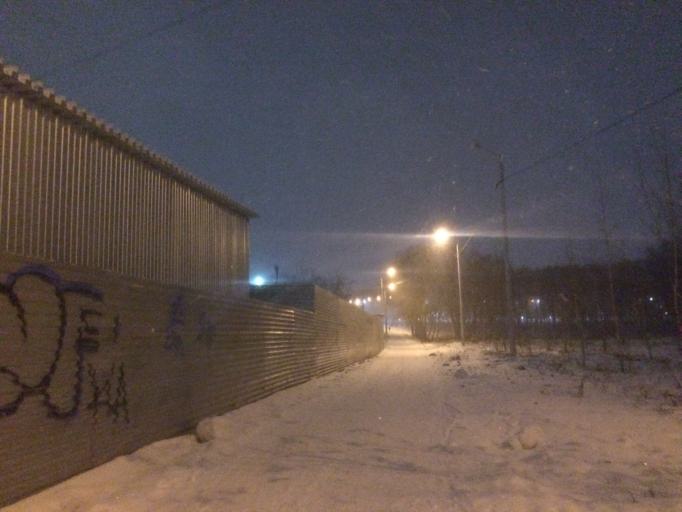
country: RU
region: Tula
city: Tula
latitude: 54.1760
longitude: 37.5907
